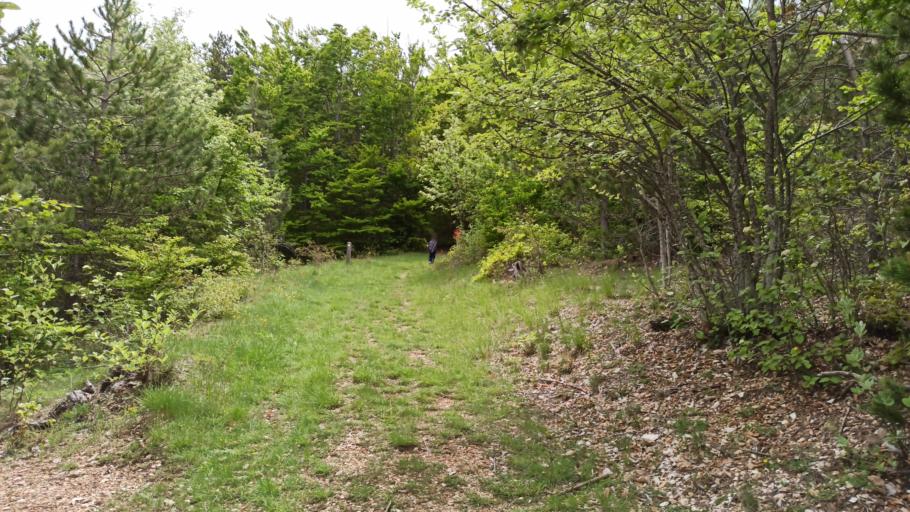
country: FR
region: Provence-Alpes-Cote d'Azur
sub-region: Departement du Vaucluse
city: Sault
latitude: 44.1419
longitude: 5.3459
